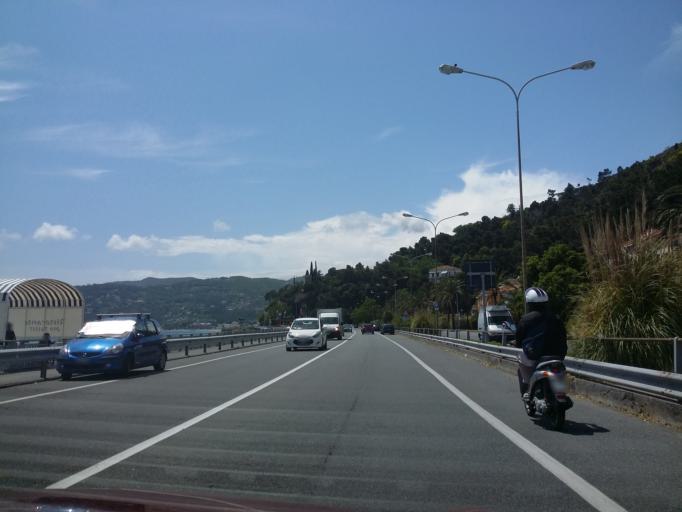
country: IT
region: Liguria
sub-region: Provincia di Savona
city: Spotorno
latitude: 44.2354
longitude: 8.4315
